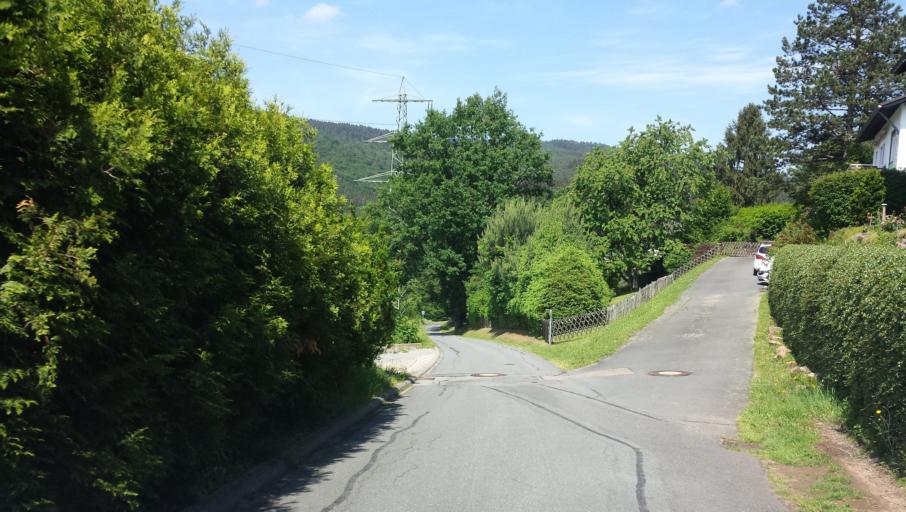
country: DE
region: Hesse
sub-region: Regierungsbezirk Darmstadt
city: Rothenberg
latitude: 49.4948
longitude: 8.9035
